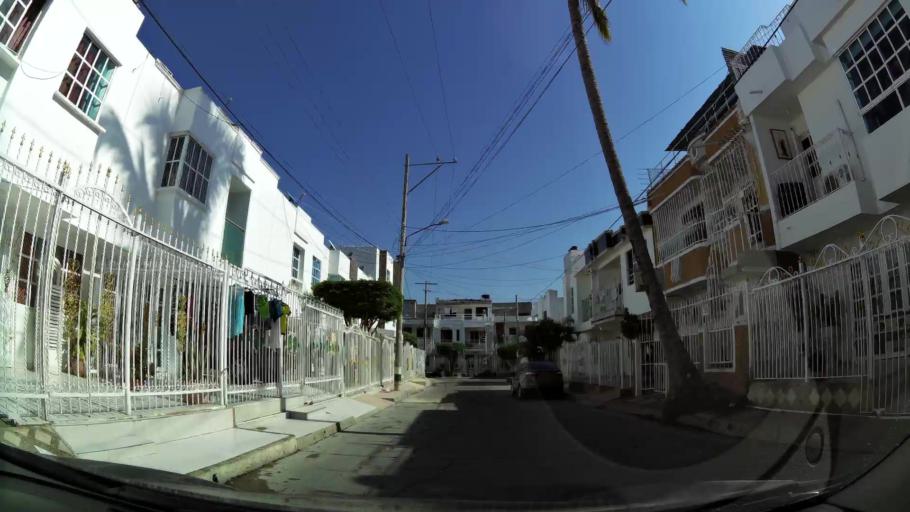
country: CO
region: Bolivar
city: Cartagena
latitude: 10.3861
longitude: -75.4686
